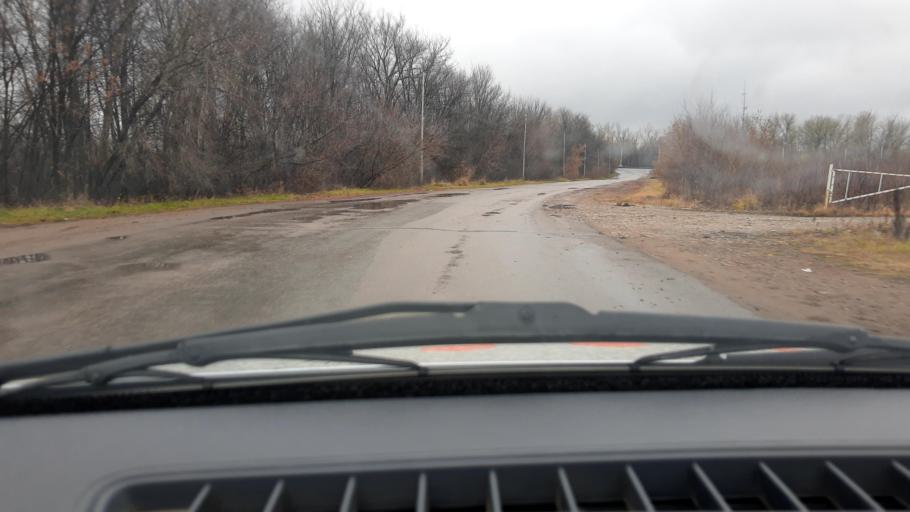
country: RU
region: Bashkortostan
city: Iglino
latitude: 54.7976
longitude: 56.2110
